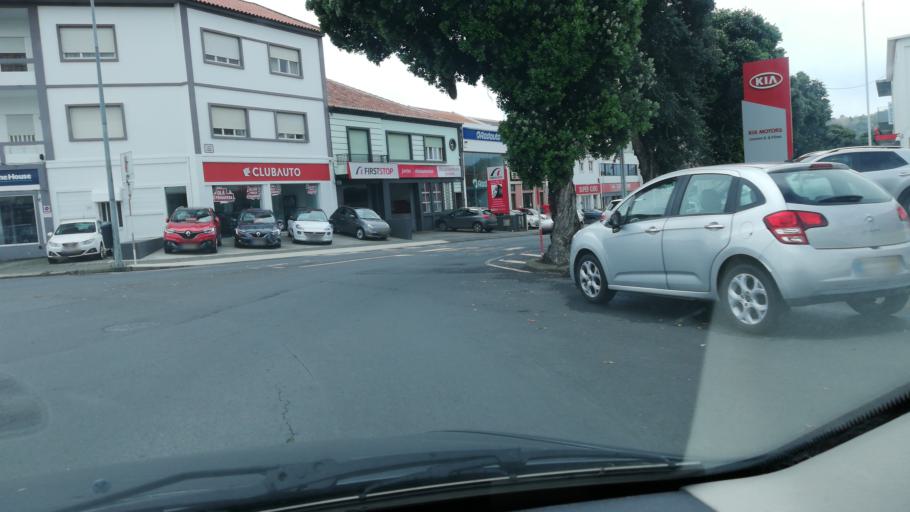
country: PT
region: Azores
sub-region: Angra do Heroismo
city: Angra do Heroismo
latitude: 38.6566
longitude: -27.2102
